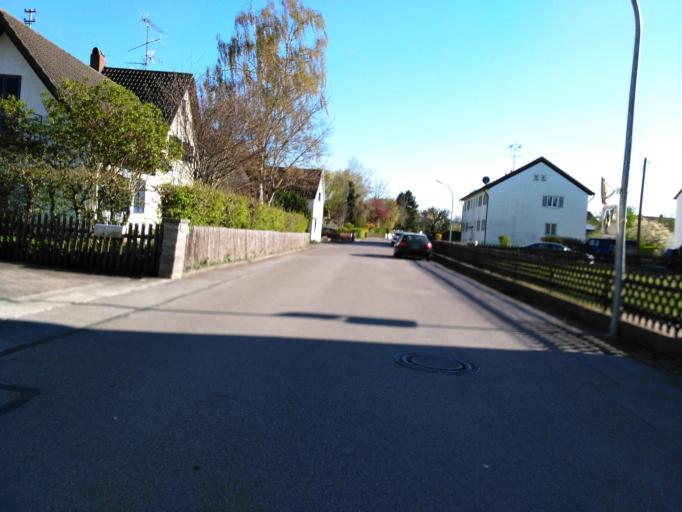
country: DE
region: Bavaria
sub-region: Upper Bavaria
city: Mammendorf
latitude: 48.2149
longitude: 11.1760
